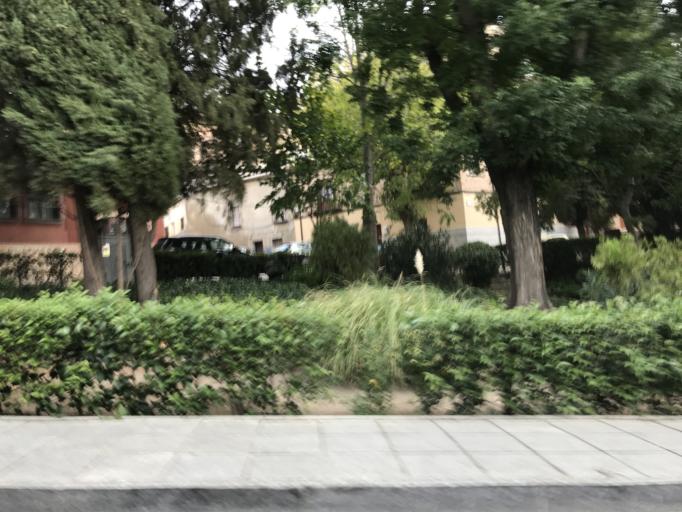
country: ES
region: Castille-La Mancha
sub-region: Province of Toledo
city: Toledo
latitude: 39.8582
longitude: -4.0332
